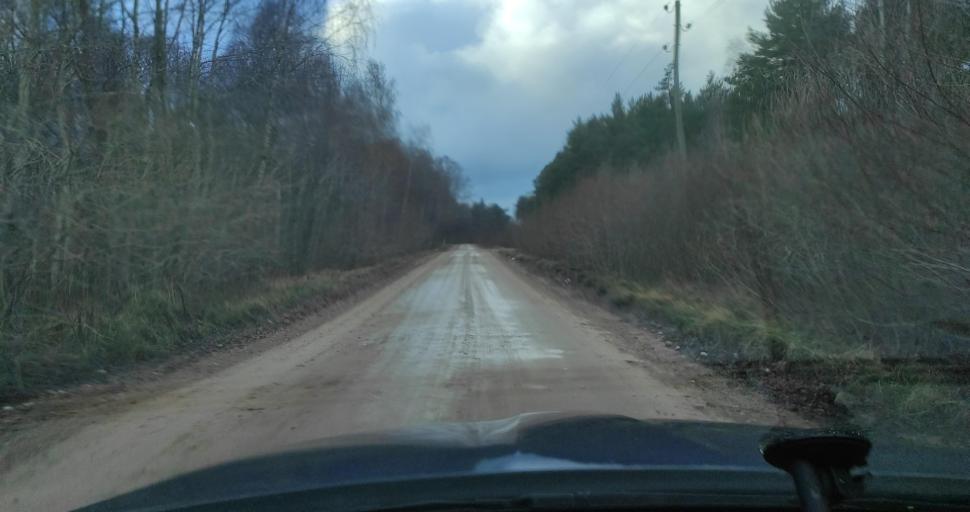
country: LV
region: Pavilostas
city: Pavilosta
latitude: 56.8563
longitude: 21.1420
